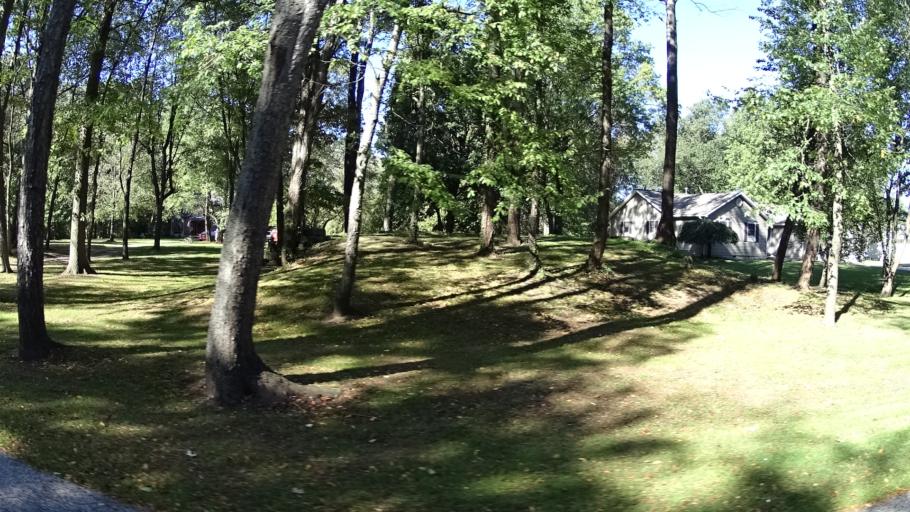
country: US
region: Ohio
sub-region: Lorain County
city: Amherst
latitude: 41.4064
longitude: -82.2527
